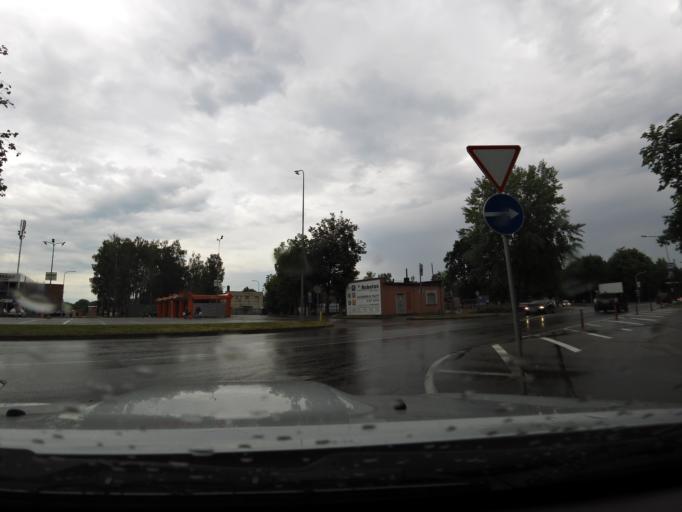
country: LT
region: Marijampoles apskritis
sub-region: Marijampole Municipality
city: Marijampole
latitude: 54.5463
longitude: 23.3476
